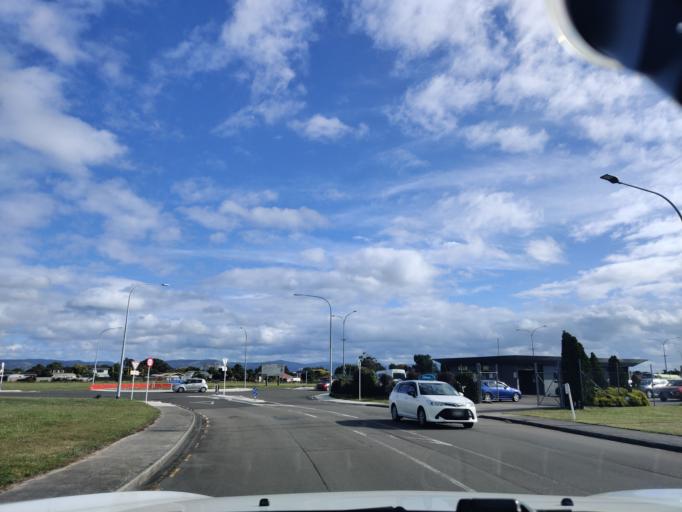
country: NZ
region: Manawatu-Wanganui
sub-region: Palmerston North City
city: Palmerston North
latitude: -40.3253
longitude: 175.6208
